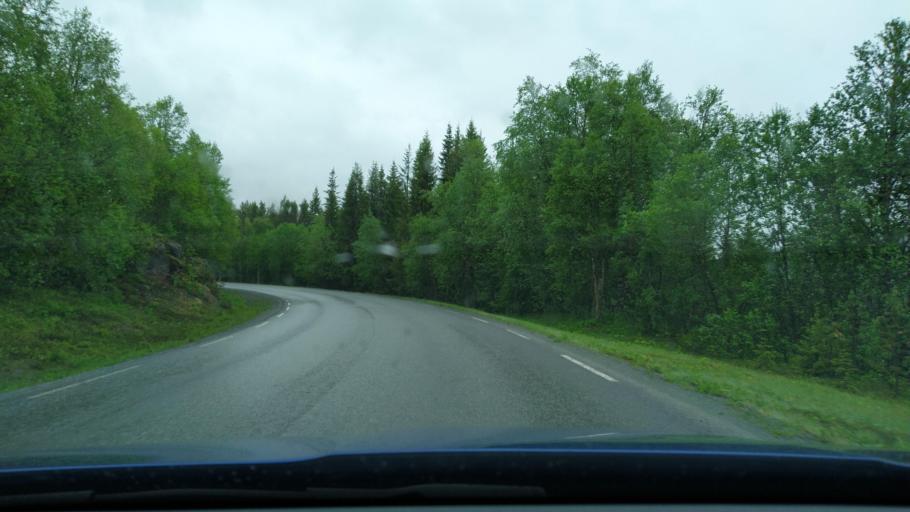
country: NO
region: Troms
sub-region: Dyroy
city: Brostadbotn
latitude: 69.0732
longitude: 17.7122
